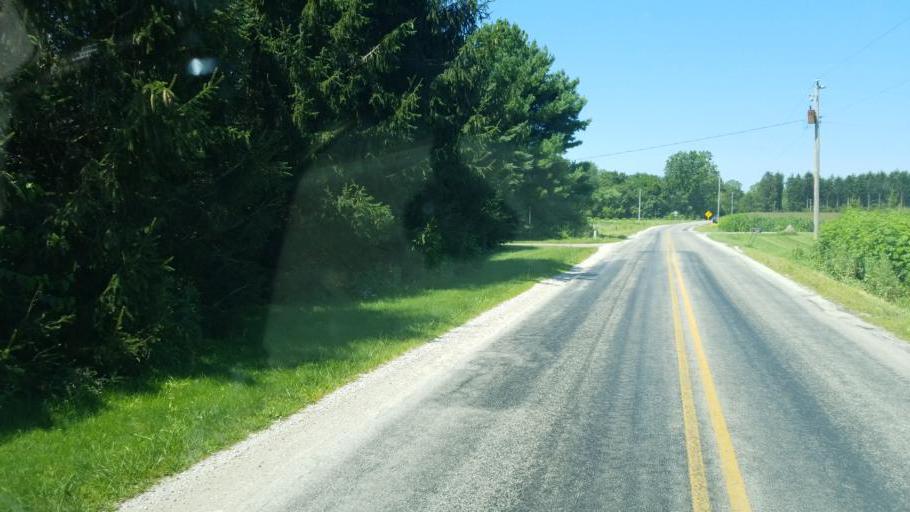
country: US
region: Ohio
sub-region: Delaware County
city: Ashley
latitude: 40.4584
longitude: -83.0657
